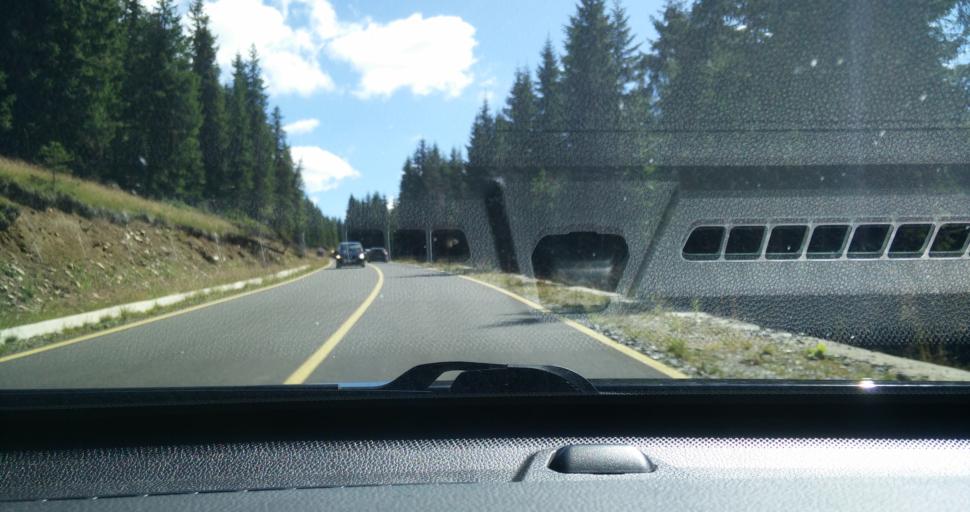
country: RO
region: Hunedoara
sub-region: Oras Petrila
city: Petrila
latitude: 45.4657
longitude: 23.6228
